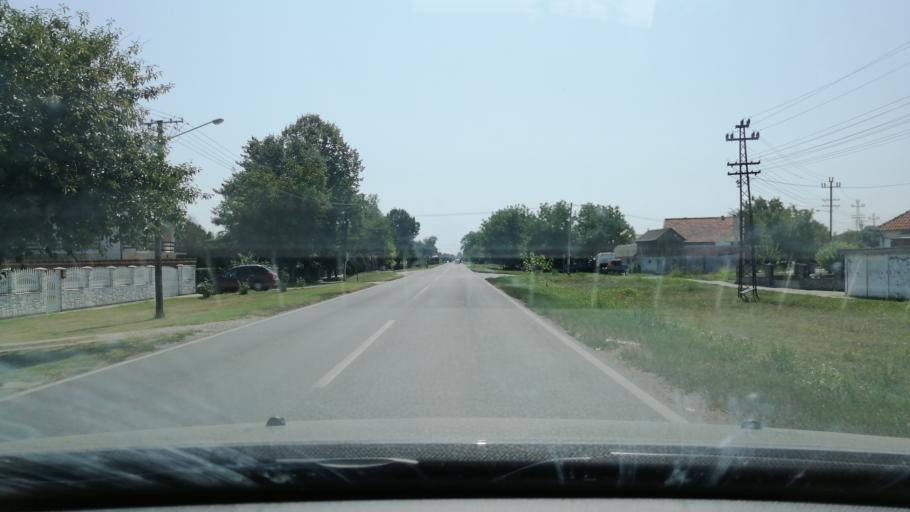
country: RS
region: Central Serbia
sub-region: Belgrade
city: Grocka
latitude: 44.7739
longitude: 20.7258
